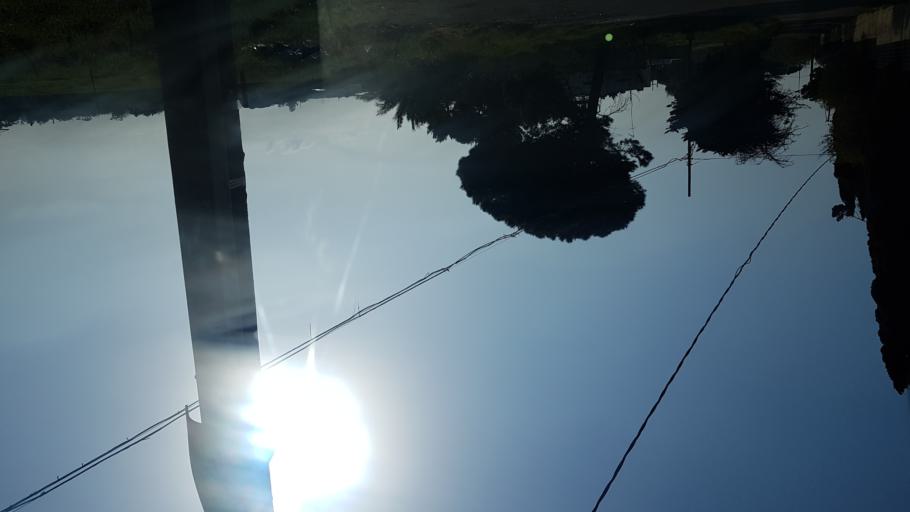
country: IT
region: Apulia
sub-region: Provincia di Brindisi
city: Materdomini
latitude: 40.6692
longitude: 17.9423
